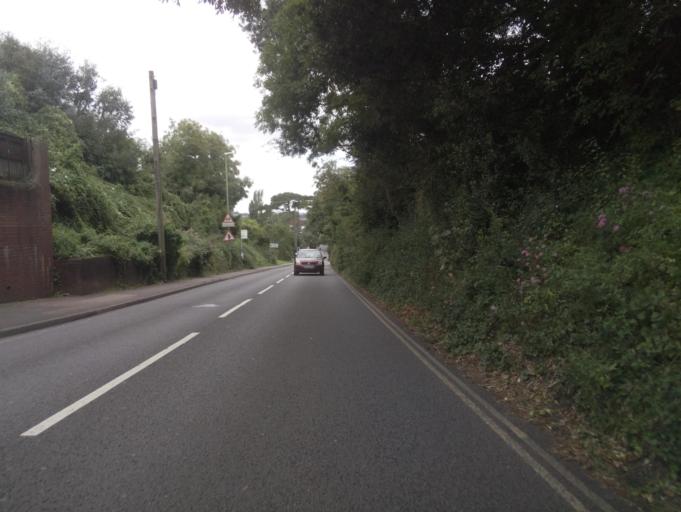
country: GB
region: England
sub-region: Borough of Torbay
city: Paignton
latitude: 50.4203
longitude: -3.5620
